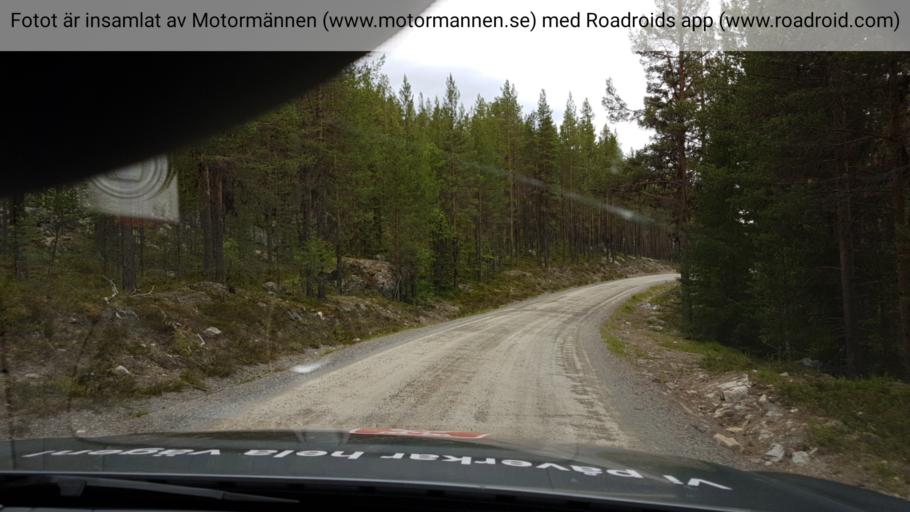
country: SE
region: Jaemtland
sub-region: Bergs Kommun
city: Hoverberg
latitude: 62.7844
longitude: 13.8247
